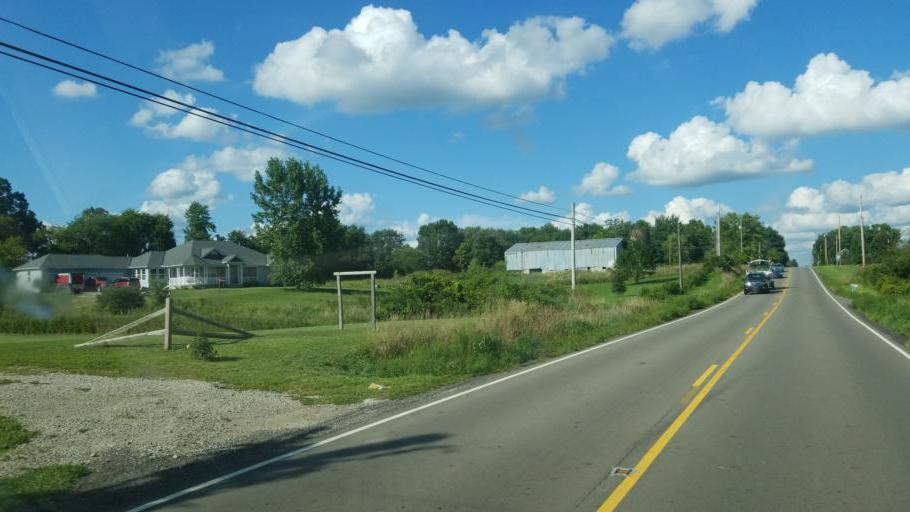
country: US
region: Ohio
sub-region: Knox County
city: Centerburg
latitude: 40.3213
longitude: -82.6714
